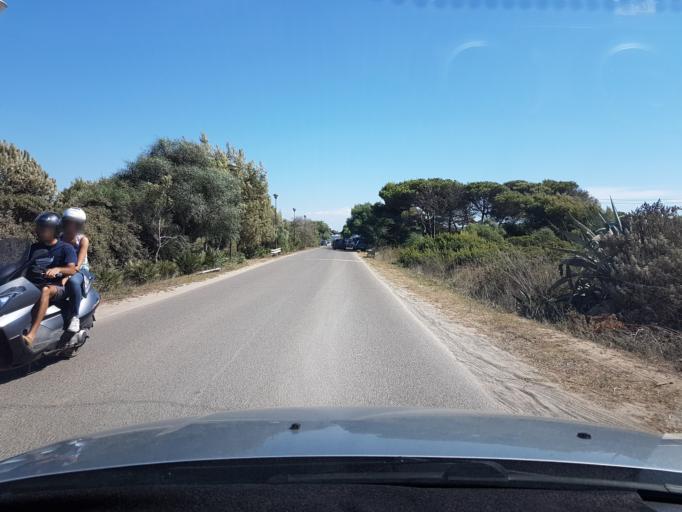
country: IT
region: Sardinia
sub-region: Provincia di Oristano
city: Cabras
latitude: 39.8867
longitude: 8.4366
